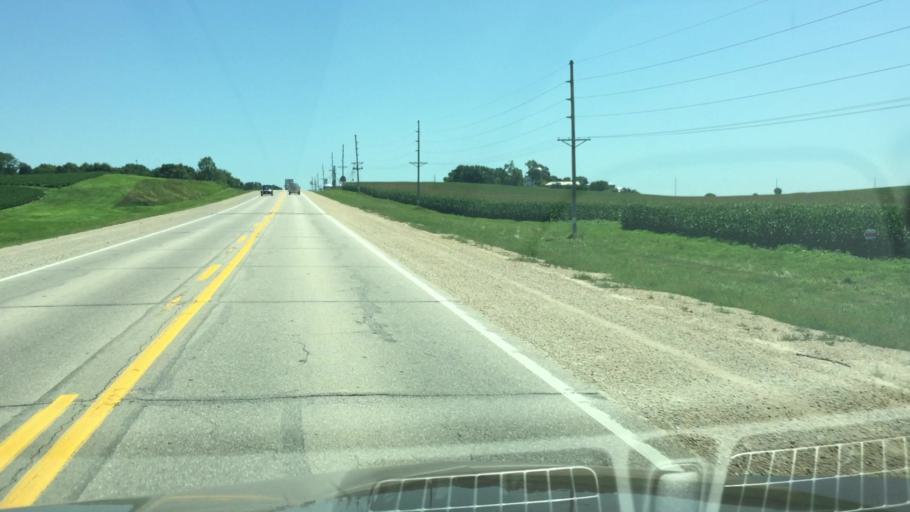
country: US
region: Iowa
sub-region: Cedar County
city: Mechanicsville
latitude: 41.8884
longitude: -91.1612
